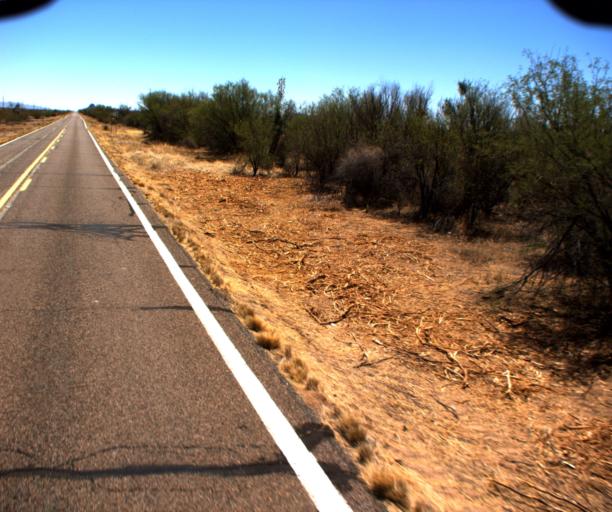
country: US
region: Arizona
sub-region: Pima County
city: Ajo
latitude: 32.2092
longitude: -112.6144
